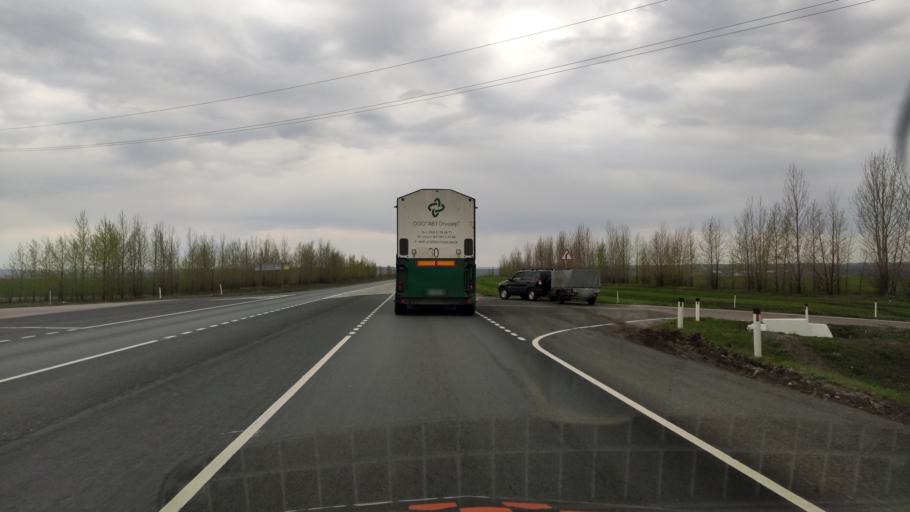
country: RU
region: Voronezj
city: Nizhnedevitsk
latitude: 51.6019
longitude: 38.6034
